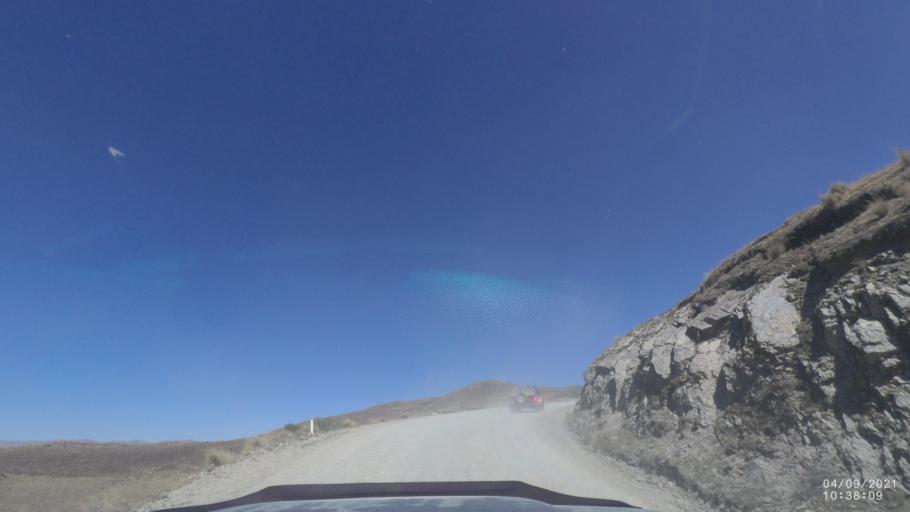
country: BO
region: Cochabamba
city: Sipe Sipe
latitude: -17.2875
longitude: -66.4565
